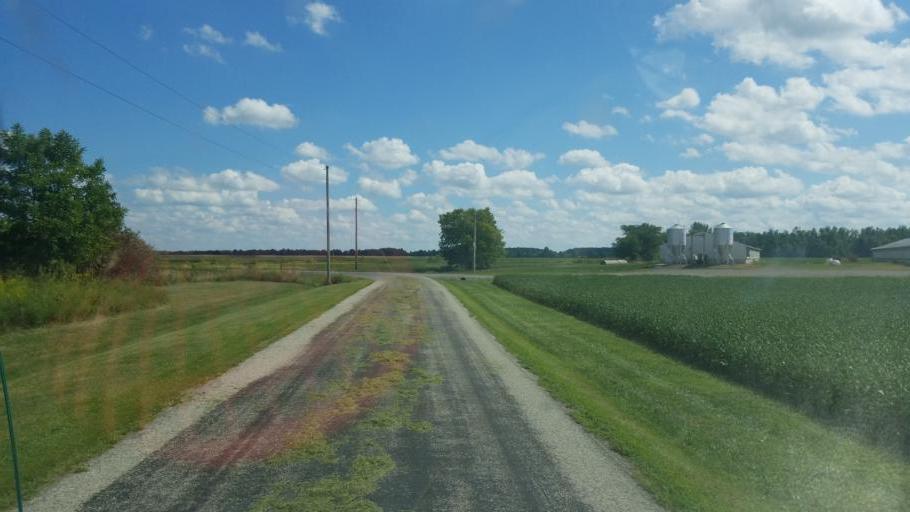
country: US
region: Ohio
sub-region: Marion County
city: Prospect
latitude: 40.3606
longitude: -83.2048
